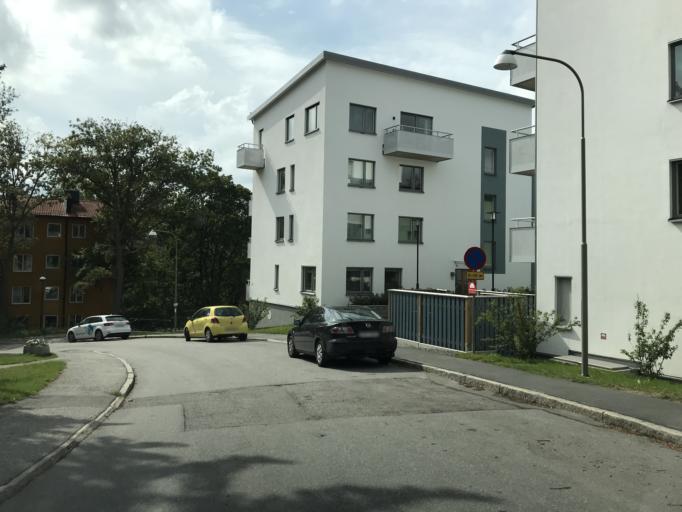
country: SE
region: Stockholm
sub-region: Sundbybergs Kommun
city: Sundbyberg
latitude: 59.3375
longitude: 17.9768
